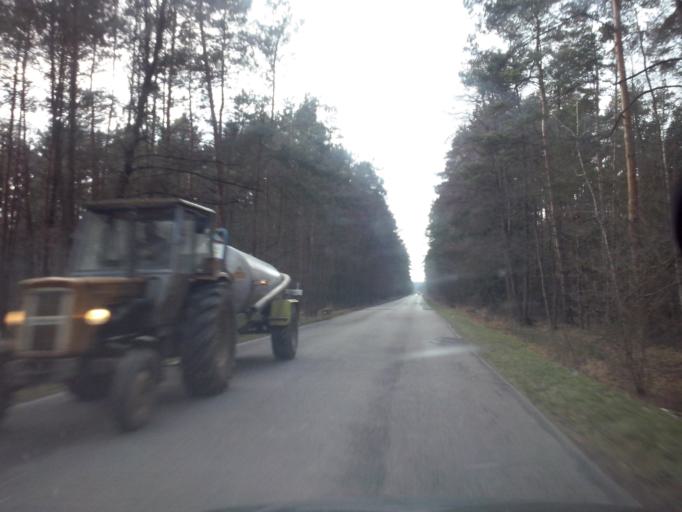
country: PL
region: Subcarpathian Voivodeship
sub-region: Powiat nizanski
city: Harasiuki
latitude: 50.4697
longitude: 22.4542
